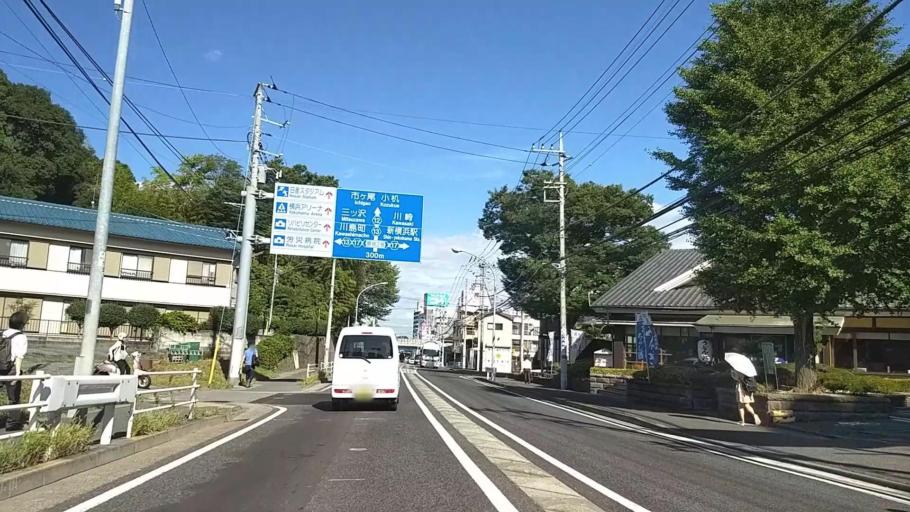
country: JP
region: Kanagawa
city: Yokohama
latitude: 35.4995
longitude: 139.6115
